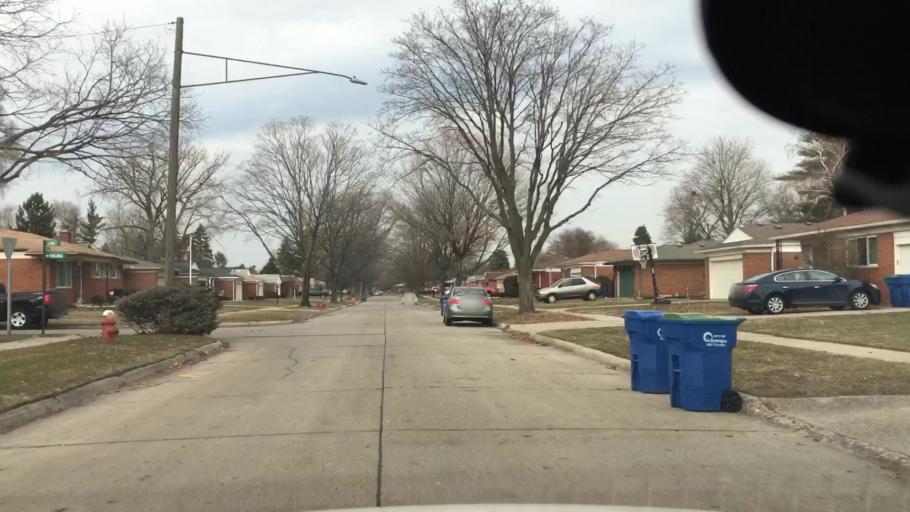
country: US
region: Michigan
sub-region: Oakland County
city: Madison Heights
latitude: 42.4920
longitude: -83.0712
